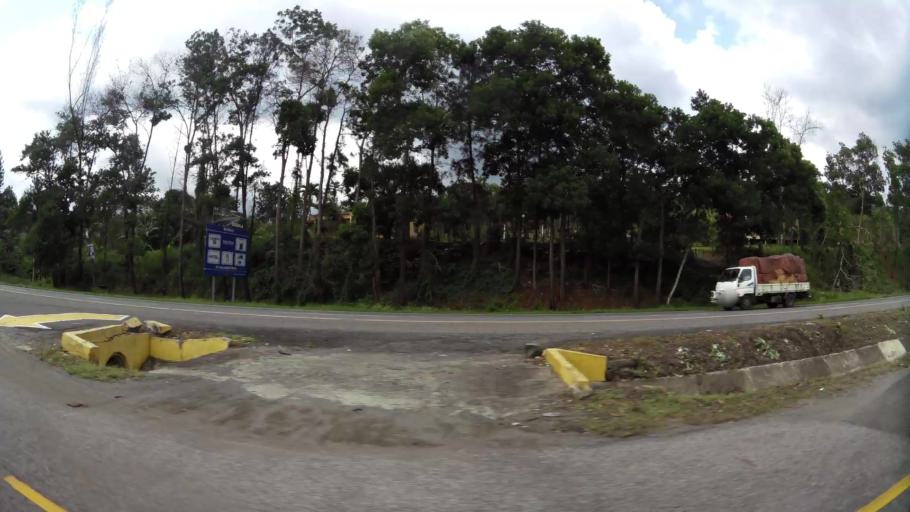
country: DO
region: Monsenor Nouel
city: Juan Adrian
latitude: 18.7830
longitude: -70.2608
